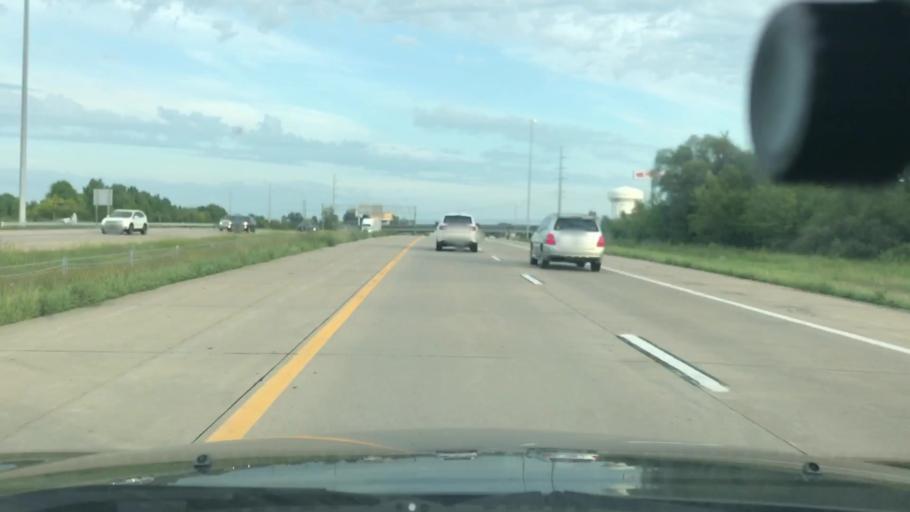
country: US
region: Missouri
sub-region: Saint Charles County
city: Lake Saint Louis
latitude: 38.7683
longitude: -90.7739
